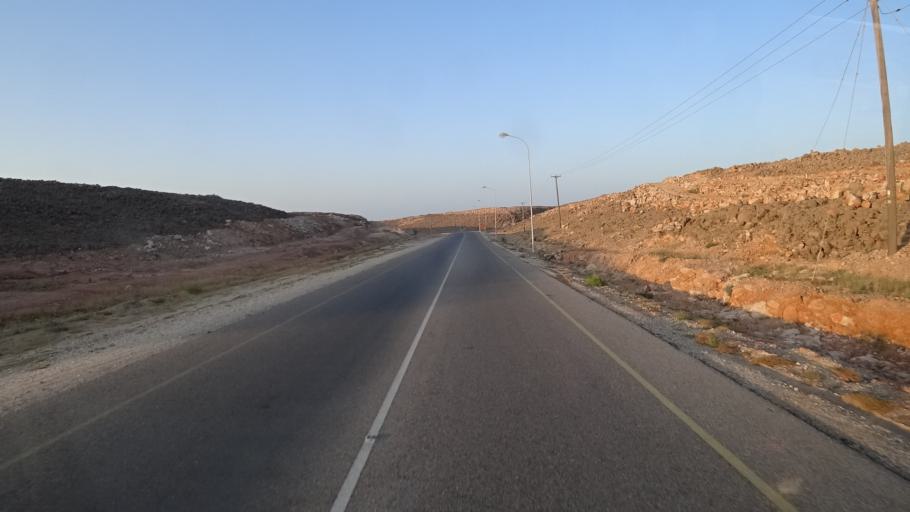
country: OM
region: Ash Sharqiyah
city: Sur
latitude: 22.4970
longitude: 59.7894
